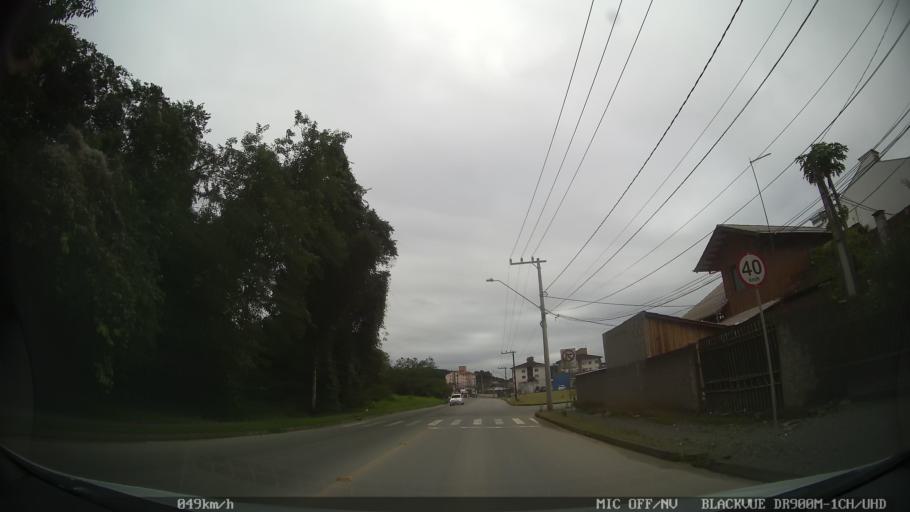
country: BR
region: Santa Catarina
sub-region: Joinville
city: Joinville
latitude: -26.2701
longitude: -48.8911
